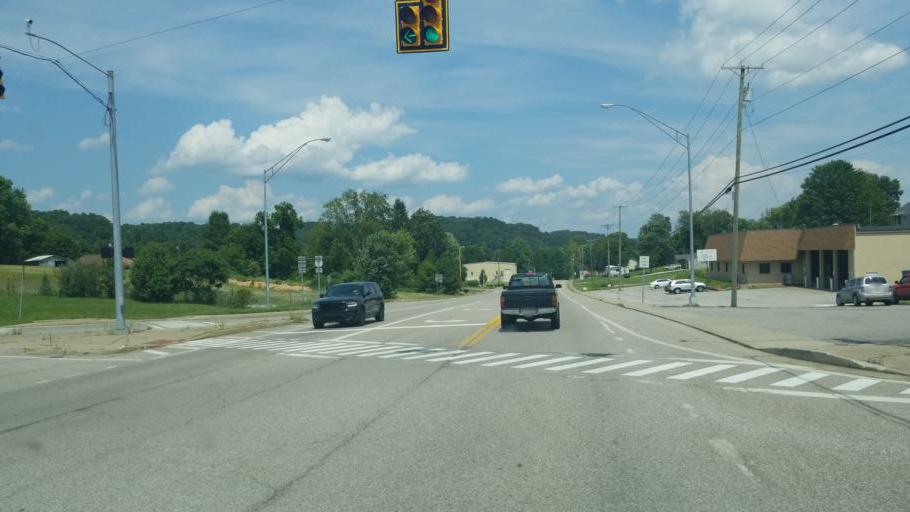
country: US
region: West Virginia
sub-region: Putnam County
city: Teays Valley
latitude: 38.4499
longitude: -81.9028
